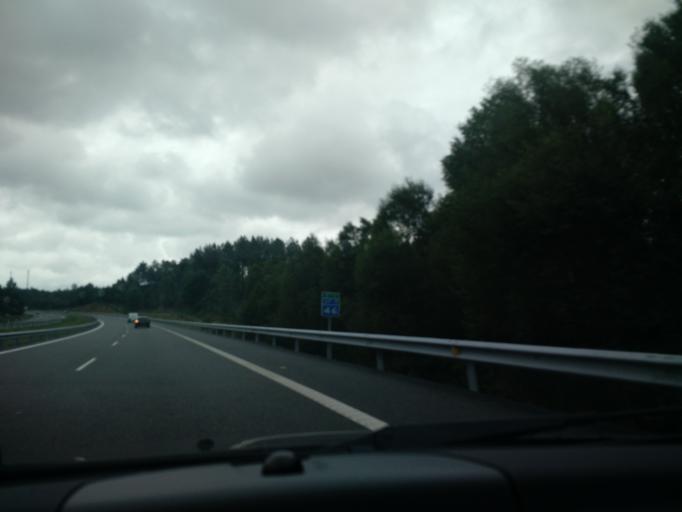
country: ES
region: Galicia
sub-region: Provincia da Coruna
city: Ordes
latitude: 43.0454
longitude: -8.3801
